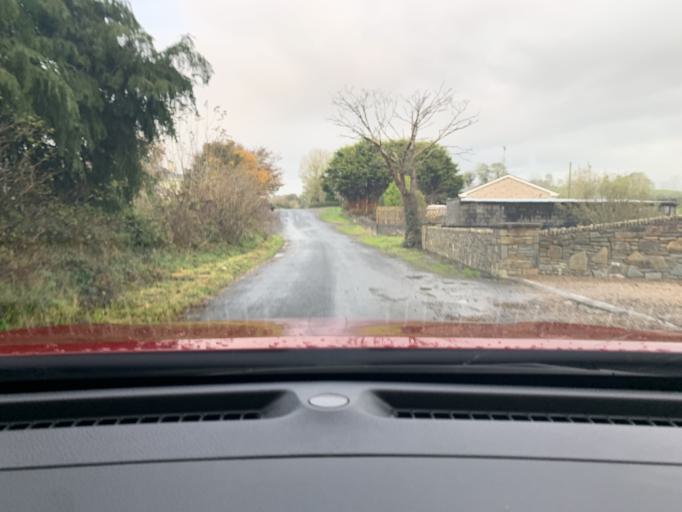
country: IE
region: Connaught
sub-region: Sligo
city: Collooney
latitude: 54.1728
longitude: -8.5109
